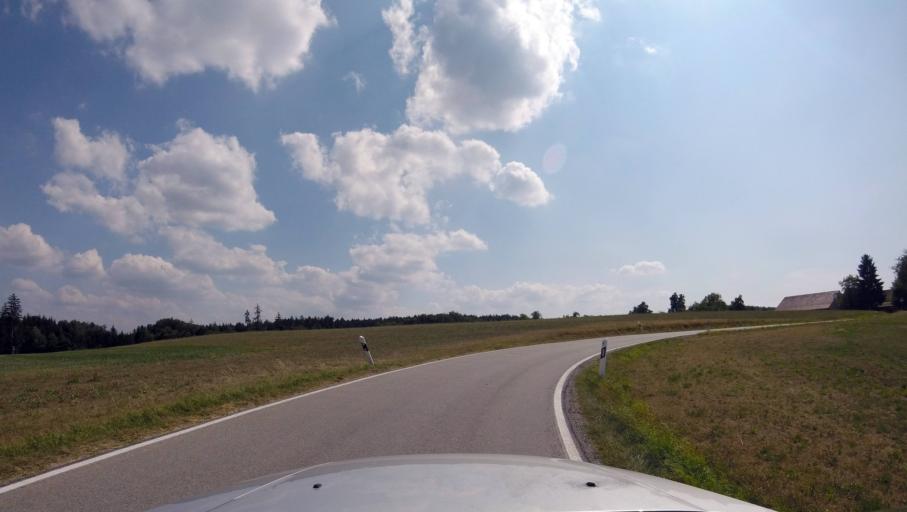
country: DE
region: Baden-Wuerttemberg
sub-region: Regierungsbezirk Stuttgart
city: Kaisersbach
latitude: 48.9498
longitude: 9.6056
